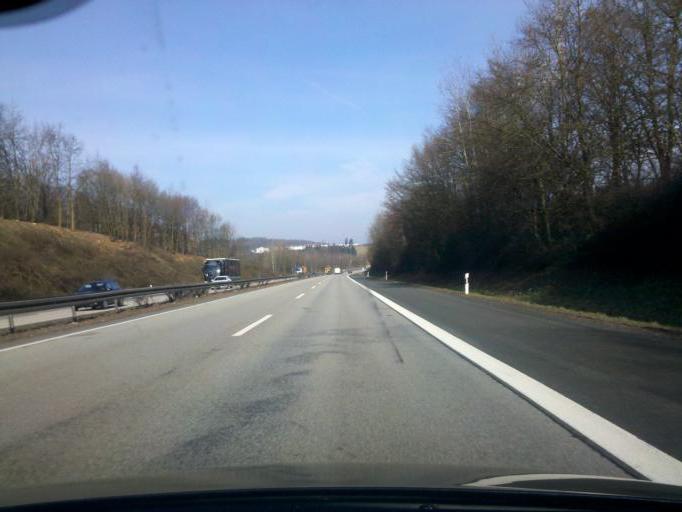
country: DE
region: North Rhine-Westphalia
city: Freudenberg
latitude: 50.8944
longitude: 7.9247
